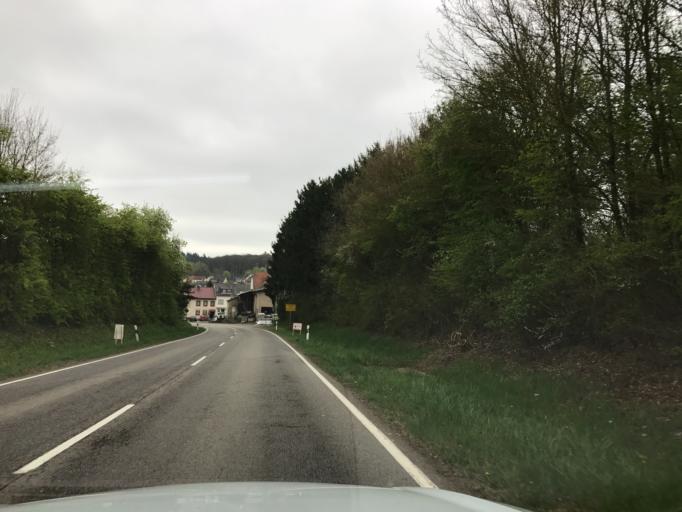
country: DE
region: Rheinland-Pfalz
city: Kirf
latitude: 49.5100
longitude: 6.4660
